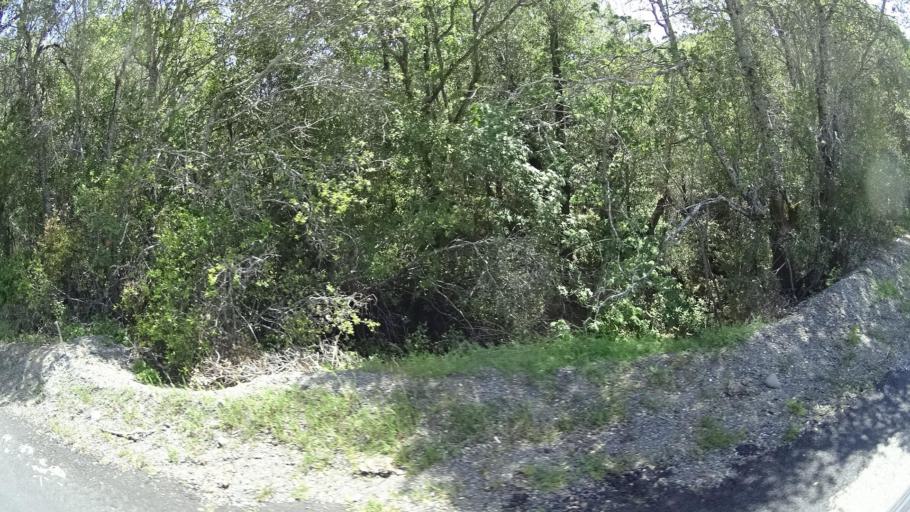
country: US
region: California
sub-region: Humboldt County
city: Redway
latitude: 40.2375
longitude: -123.6320
